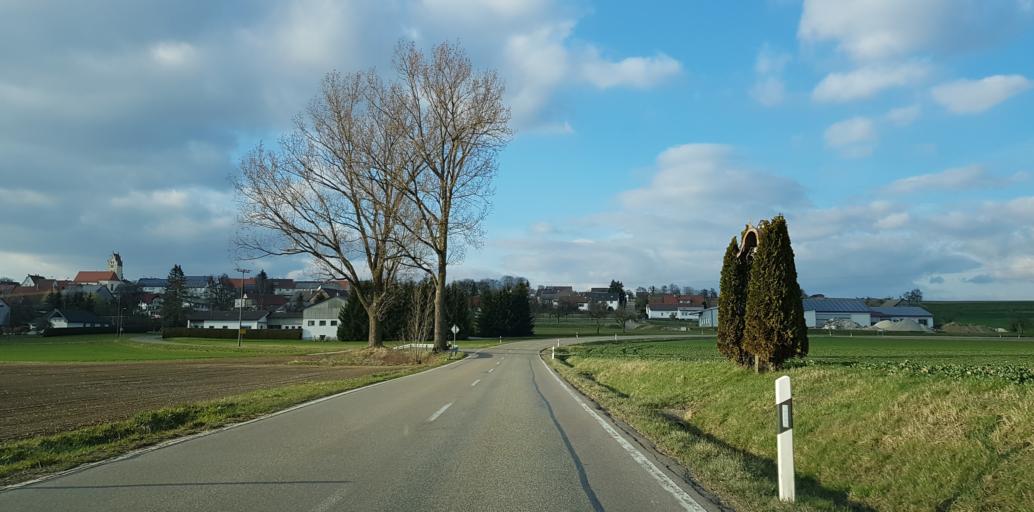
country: DE
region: Baden-Wuerttemberg
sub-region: Tuebingen Region
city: Altheim
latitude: 48.3245
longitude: 9.7751
